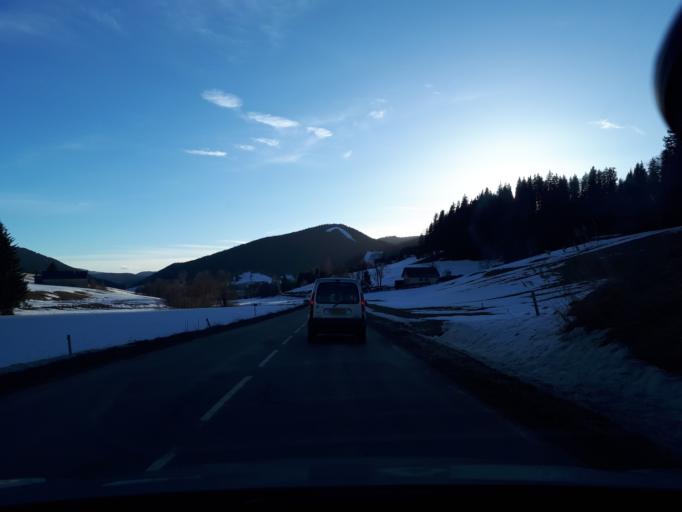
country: FR
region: Rhone-Alpes
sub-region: Departement de l'Isere
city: Meaudre
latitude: 45.1403
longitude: 5.5356
